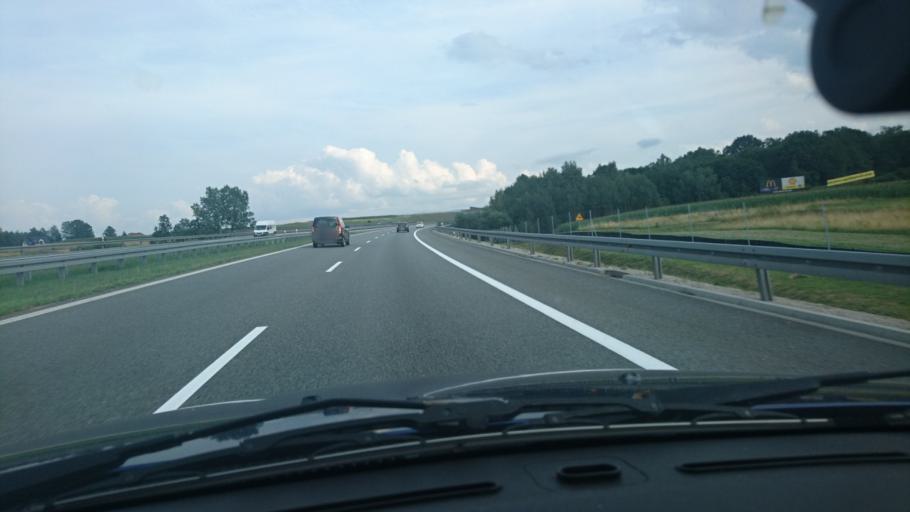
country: PL
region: Silesian Voivodeship
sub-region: Powiat zywiecki
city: Pietrzykowice
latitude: 49.6972
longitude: 19.1331
